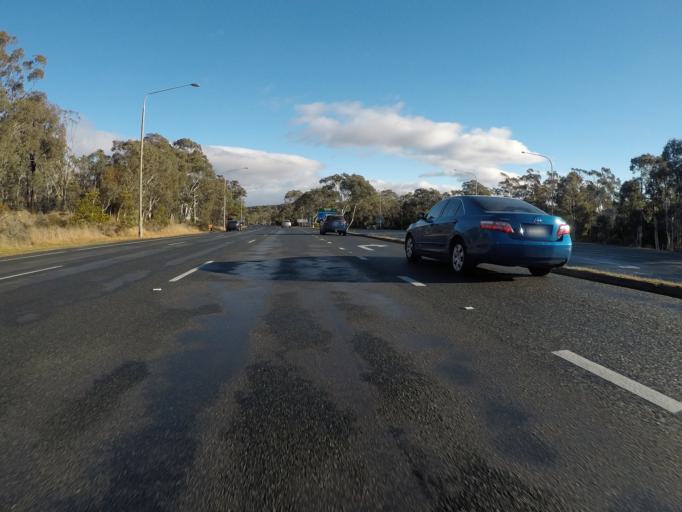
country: AU
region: Australian Capital Territory
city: Macquarie
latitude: -35.2562
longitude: 149.0885
